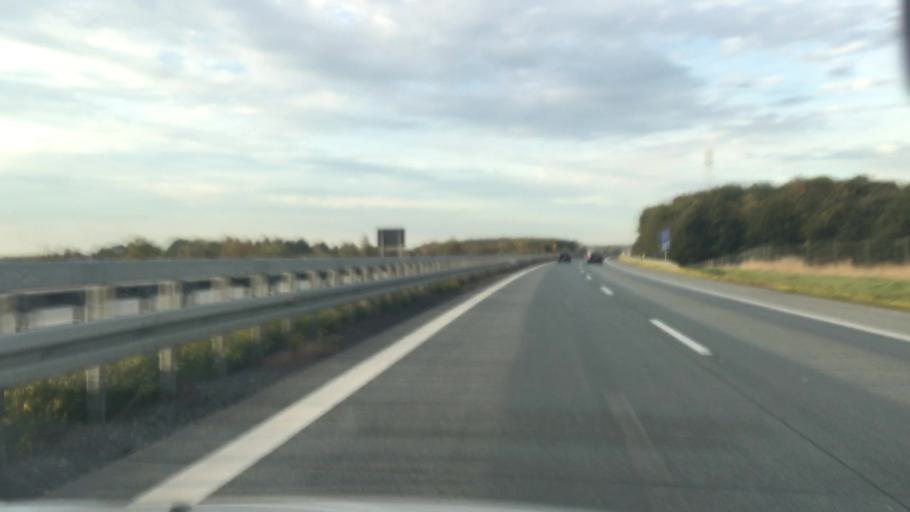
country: DE
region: Saxony
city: Schonfeld
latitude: 51.3272
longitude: 13.7185
